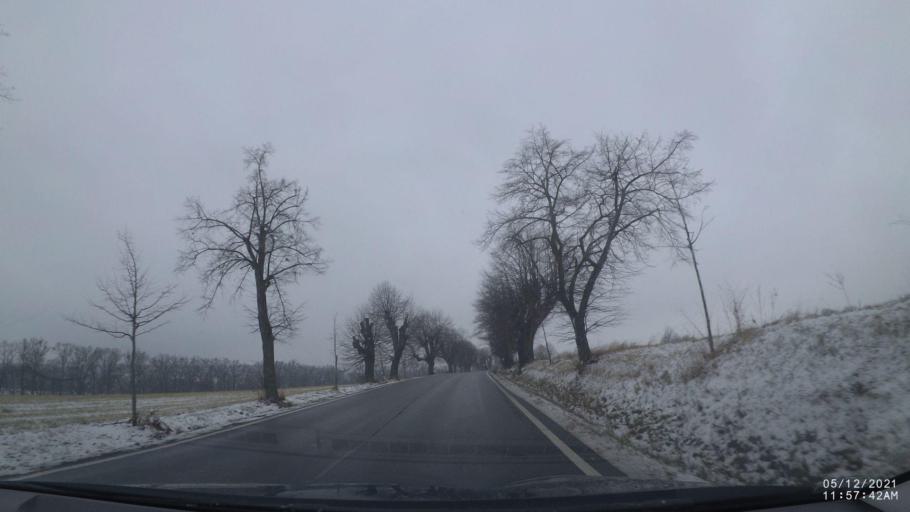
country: CZ
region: Kralovehradecky
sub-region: Okres Rychnov nad Kneznou
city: Opocno
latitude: 50.2756
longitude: 16.1316
